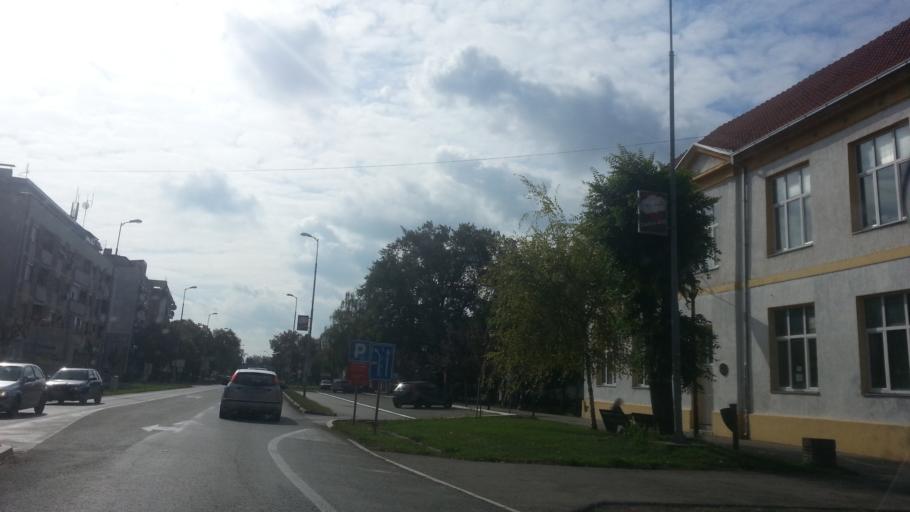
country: RS
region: Autonomna Pokrajina Vojvodina
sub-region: Sremski Okrug
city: Stara Pazova
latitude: 44.9839
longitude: 20.1591
